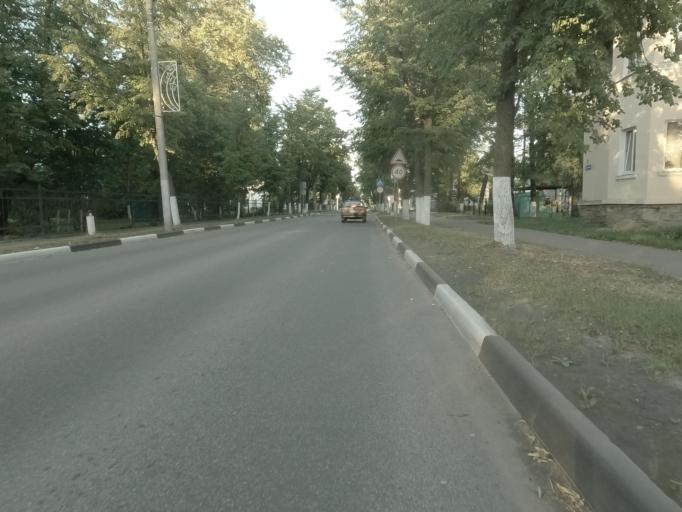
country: RU
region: Leningrad
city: Kirovsk
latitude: 59.8758
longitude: 30.9883
